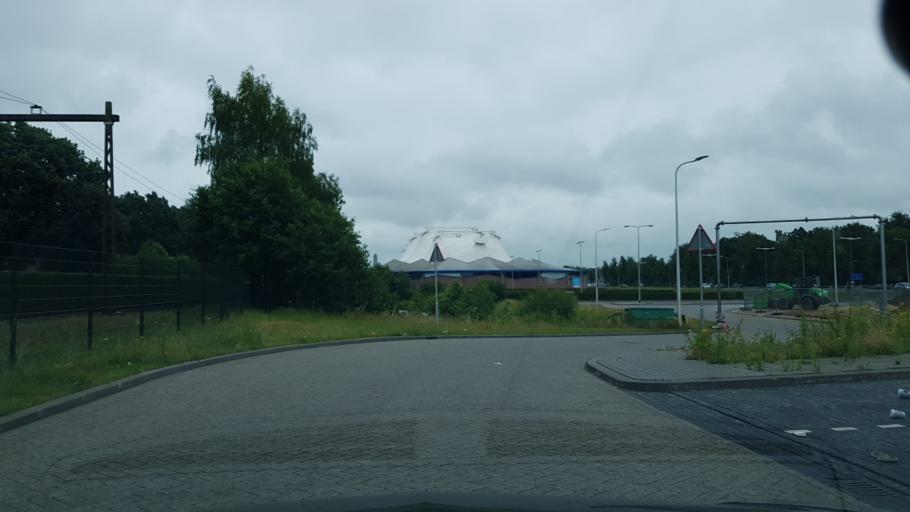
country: NL
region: Overijssel
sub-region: Gemeente Deventer
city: Schalkhaar
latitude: 52.2500
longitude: 6.2066
